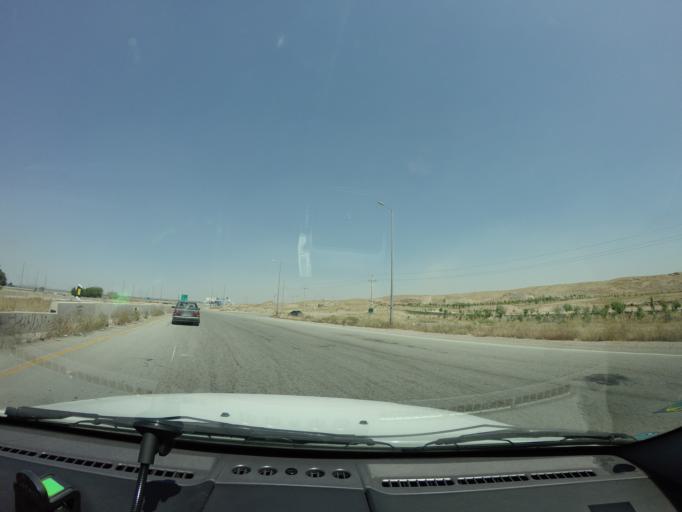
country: IR
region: Tehran
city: Eslamshahr
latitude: 35.4371
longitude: 51.2075
